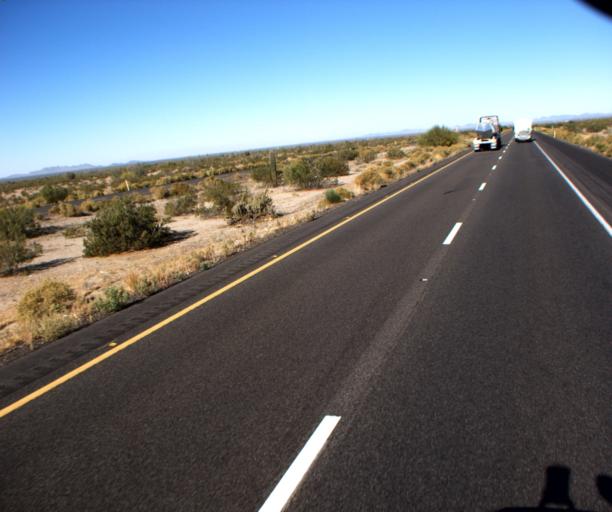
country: US
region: Arizona
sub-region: Maricopa County
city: Gila Bend
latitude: 32.9083
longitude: -112.5930
